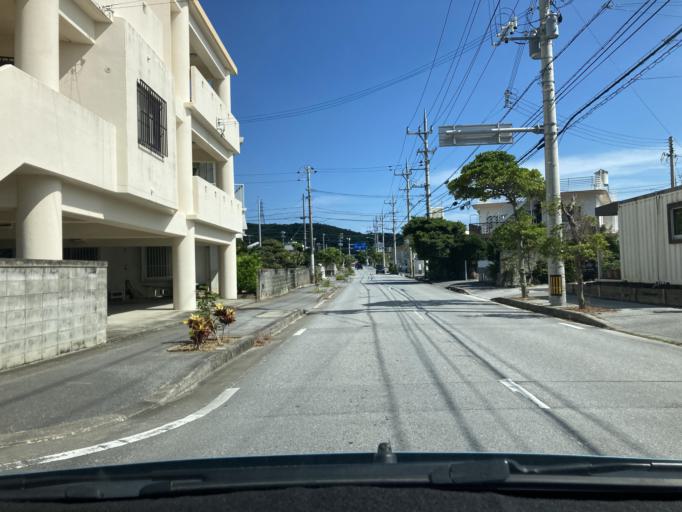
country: JP
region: Okinawa
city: Ginowan
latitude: 26.2294
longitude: 127.7520
